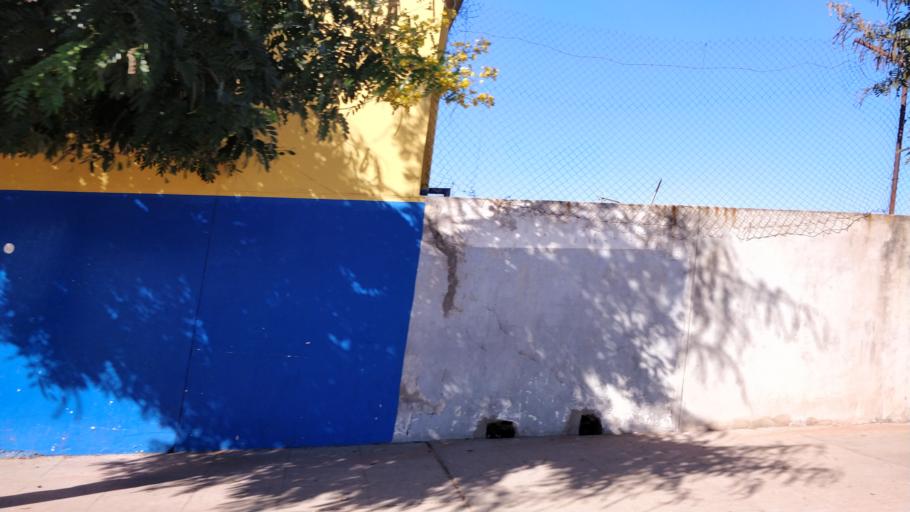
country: MZ
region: Maputo City
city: Maputo
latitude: -25.9279
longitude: 32.6015
